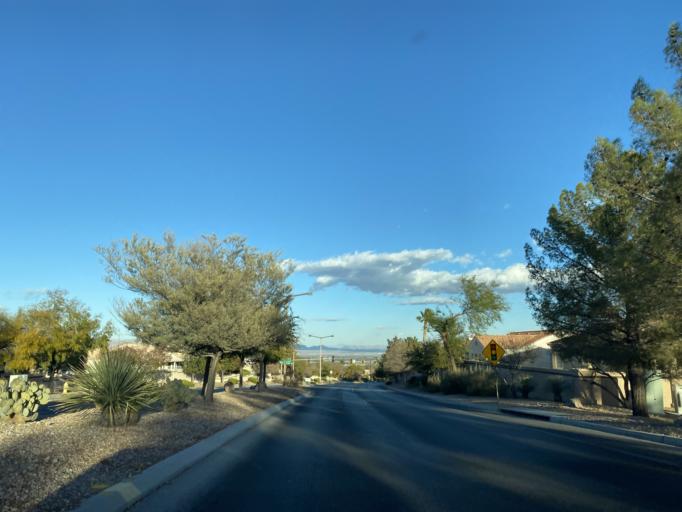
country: US
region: Nevada
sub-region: Clark County
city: Summerlin South
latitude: 36.2043
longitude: -115.3272
